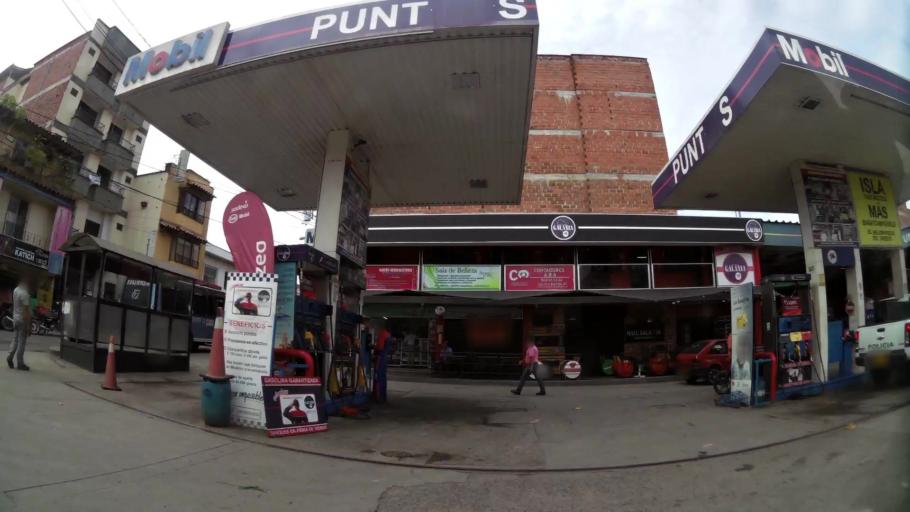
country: CO
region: Antioquia
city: Rionegro
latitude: 6.1552
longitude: -75.3719
